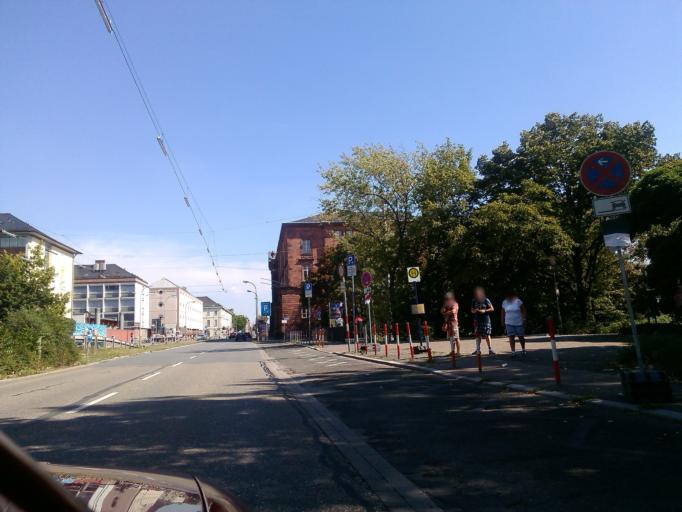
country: DE
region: Rheinland-Pfalz
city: Ludwigshafen am Rhein
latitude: 49.4860
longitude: 8.4590
